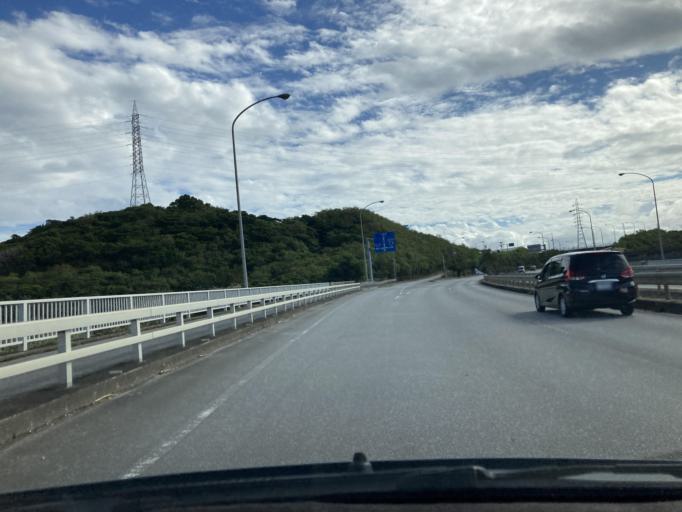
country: JP
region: Okinawa
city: Tomigusuku
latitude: 26.1766
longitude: 127.7273
